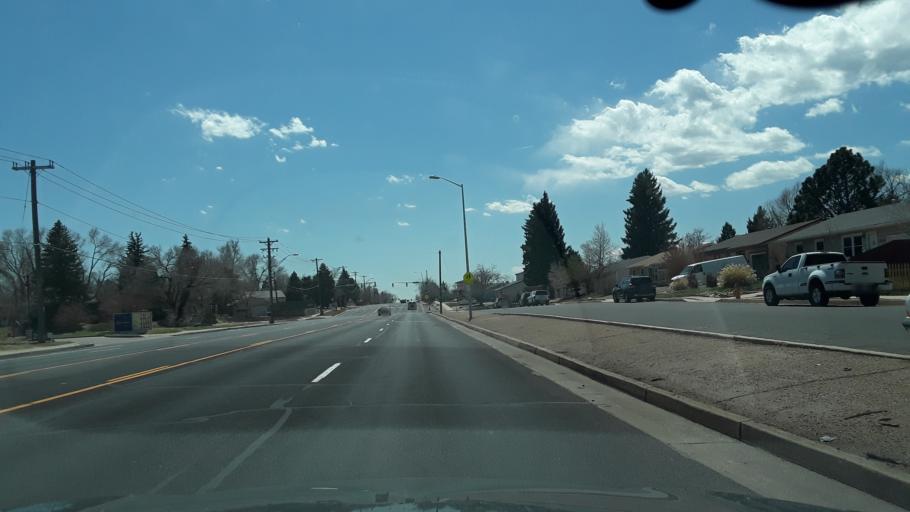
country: US
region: Colorado
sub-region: El Paso County
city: Colorado Springs
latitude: 38.8582
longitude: -104.7758
